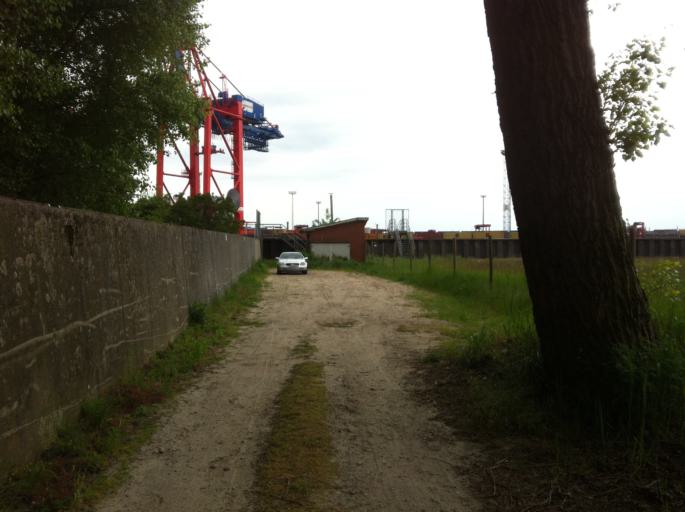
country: DE
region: Hamburg
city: Altona
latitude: 53.5370
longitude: 9.9005
